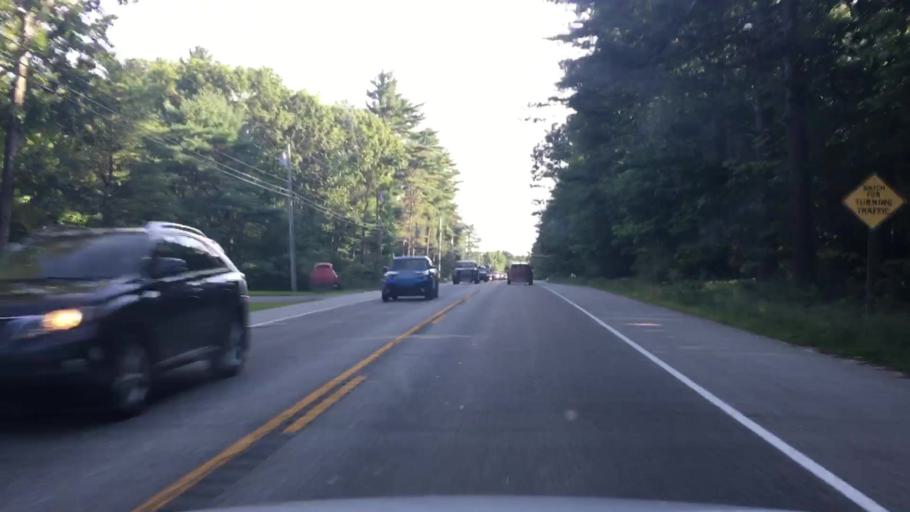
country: US
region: Maine
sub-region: Cumberland County
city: Raymond
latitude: 43.8730
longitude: -70.4647
